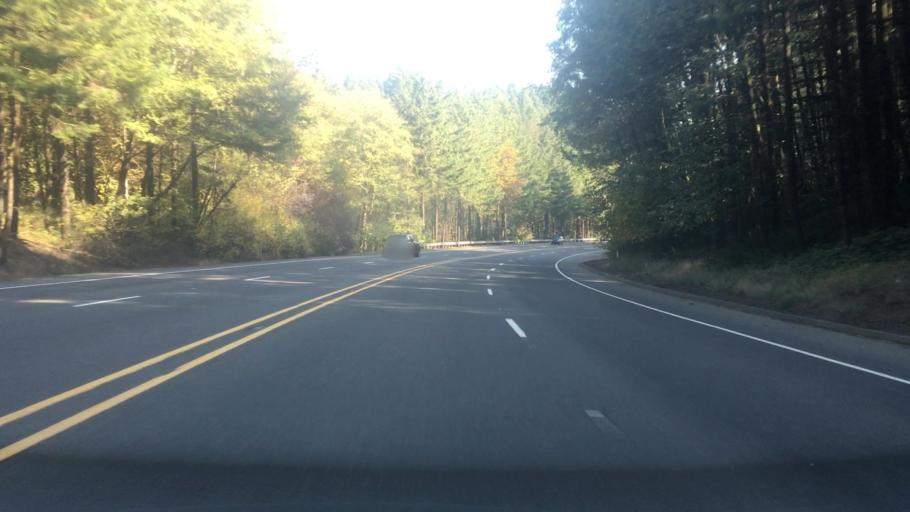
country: US
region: Oregon
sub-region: Polk County
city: Grand Ronde
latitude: 45.0610
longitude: -123.6911
